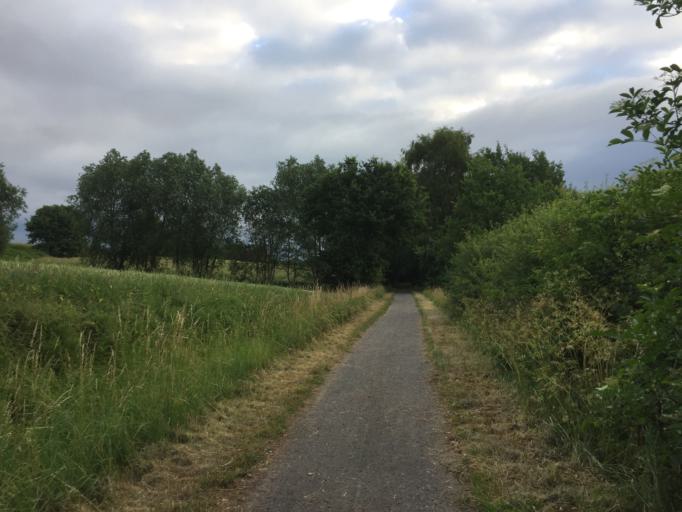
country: DE
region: Hesse
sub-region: Regierungsbezirk Kassel
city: Lohfelden
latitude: 51.2519
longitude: 9.5570
